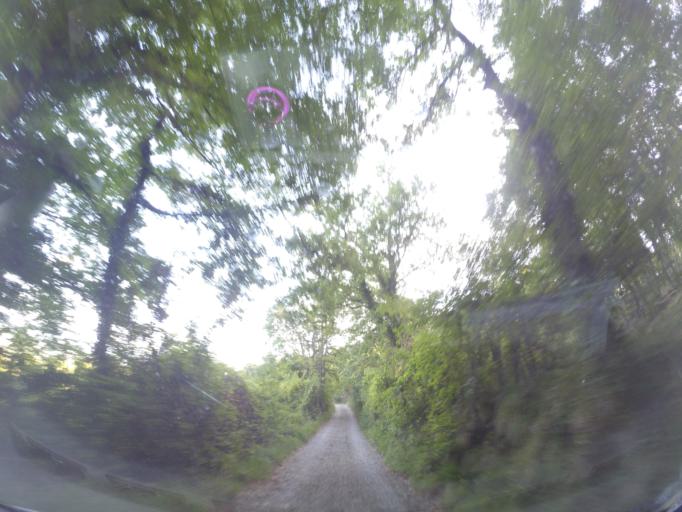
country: IT
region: Tuscany
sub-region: Province of Arezzo
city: Talla
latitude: 43.5631
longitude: 11.7845
